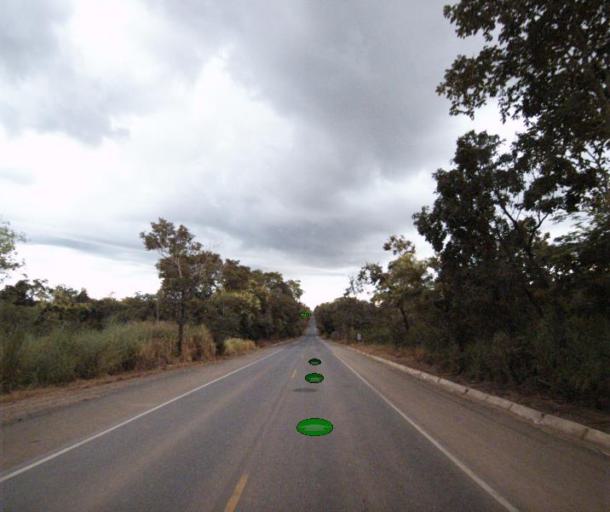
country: BR
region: Goias
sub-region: Uruacu
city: Uruacu
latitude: -14.6926
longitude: -49.2135
